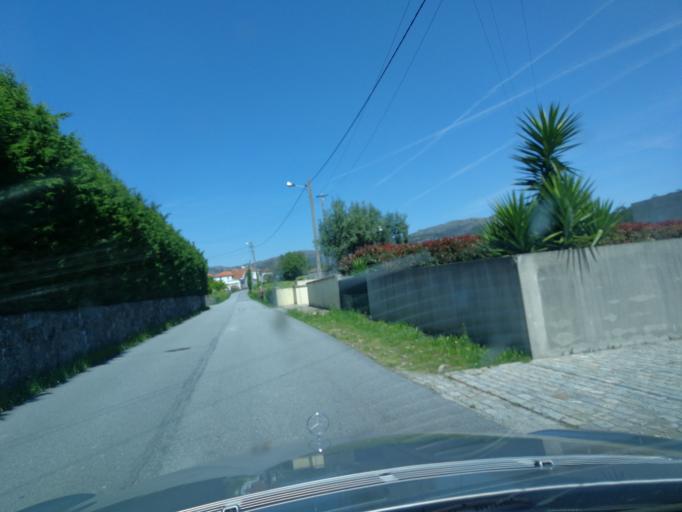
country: PT
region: Viana do Castelo
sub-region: Viana do Castelo
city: Meadela
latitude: 41.7254
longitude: -8.7903
